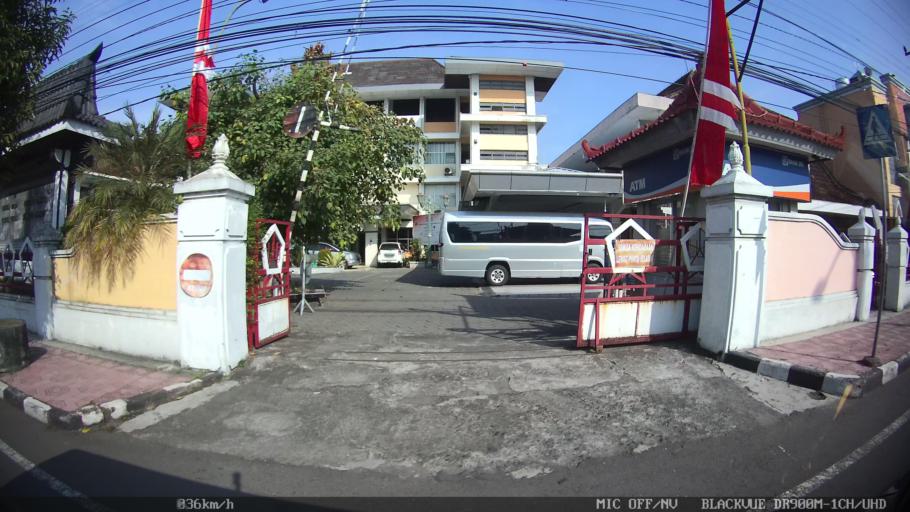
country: ID
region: Daerah Istimewa Yogyakarta
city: Yogyakarta
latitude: -7.7840
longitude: 110.3577
